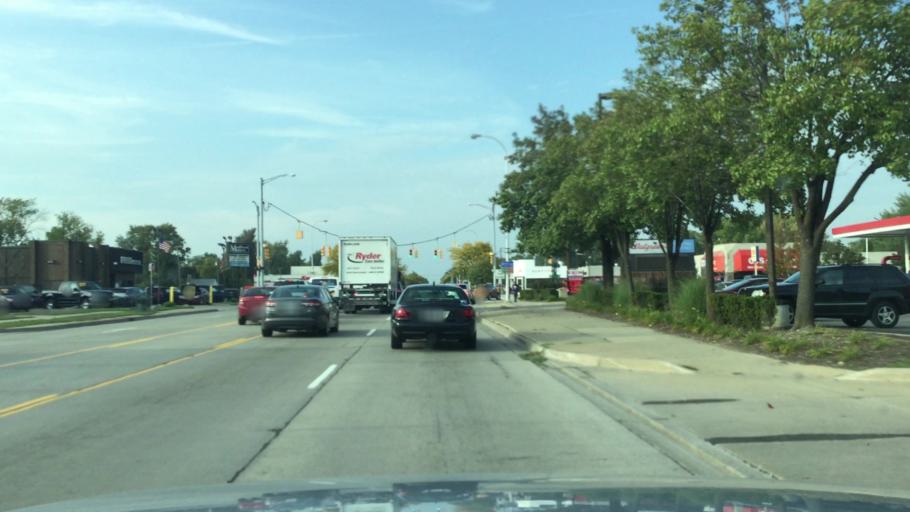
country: US
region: Michigan
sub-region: Oakland County
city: Madison Heights
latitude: 42.4899
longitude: -83.1051
